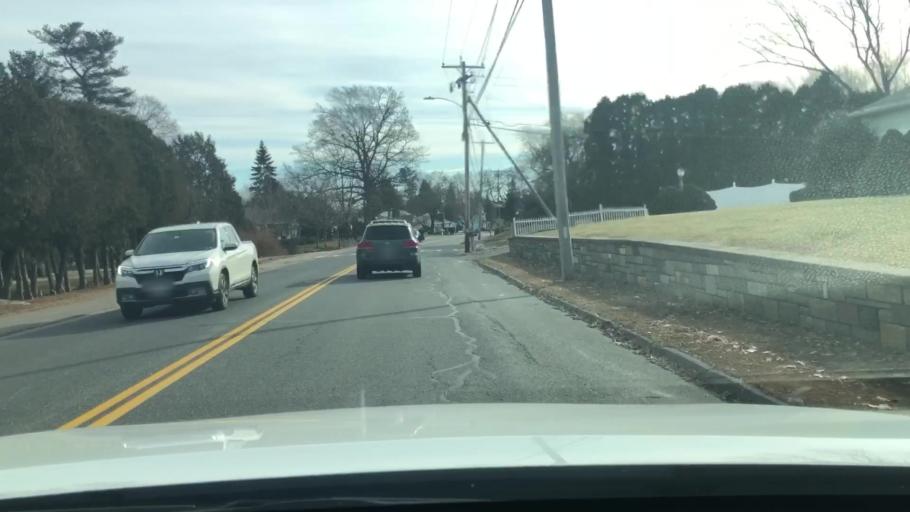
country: US
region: Massachusetts
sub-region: Worcester County
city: Hopedale
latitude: 42.1454
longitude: -71.5375
